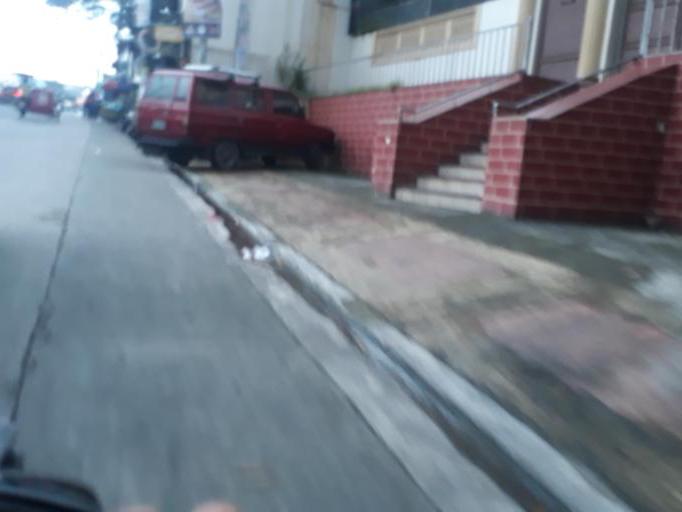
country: PH
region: Metro Manila
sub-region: Quezon City
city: Quezon City
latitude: 14.6835
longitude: 121.0782
